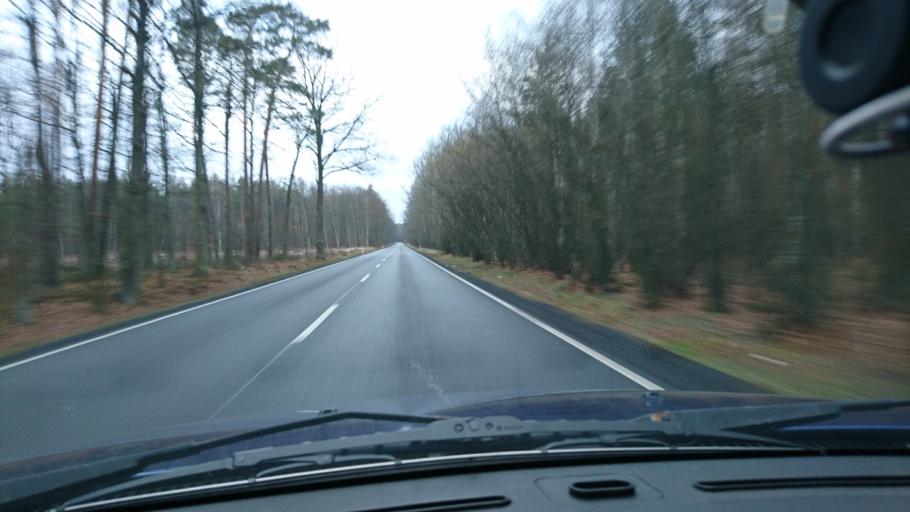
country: PL
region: Opole Voivodeship
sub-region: Powiat oleski
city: Olesno
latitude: 50.9304
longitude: 18.3339
